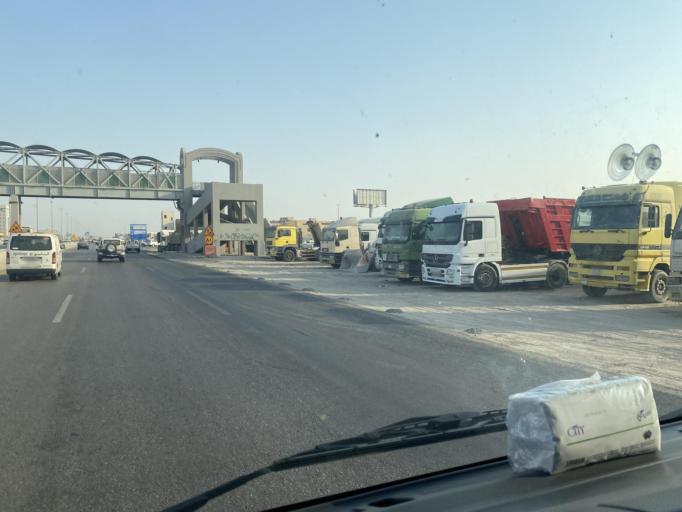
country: SA
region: Eastern Province
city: Sayhat
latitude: 26.4039
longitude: 50.0154
